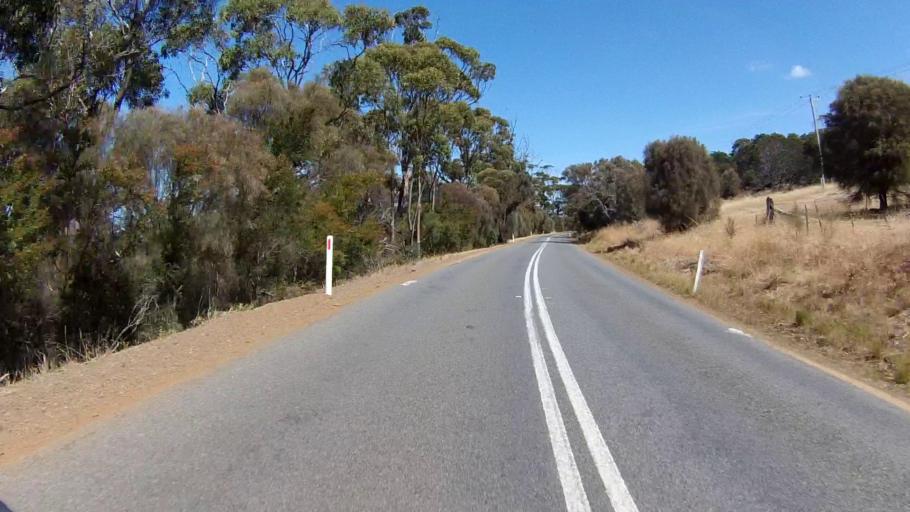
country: AU
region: Tasmania
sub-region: Sorell
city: Sorell
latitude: -42.2352
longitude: 148.0166
